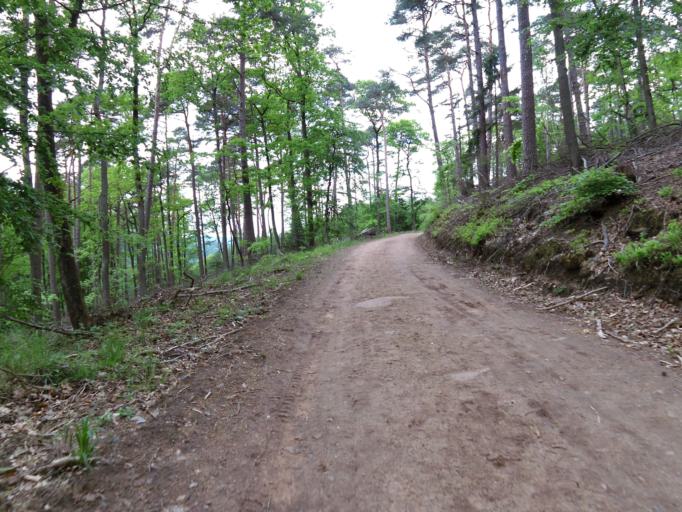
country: DE
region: Rheinland-Pfalz
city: Neidenfels
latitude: 49.4088
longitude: 8.0649
